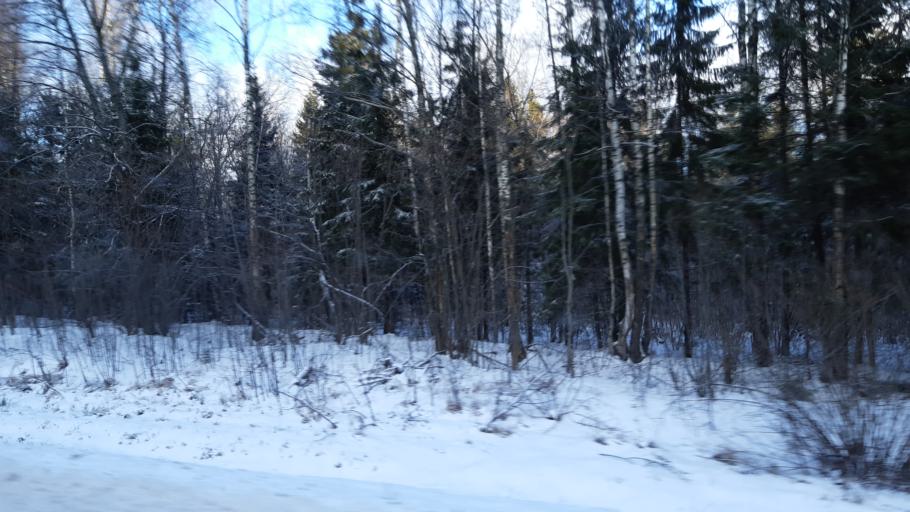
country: RU
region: Moskovskaya
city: Svatkovo
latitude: 56.3048
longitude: 38.3356
